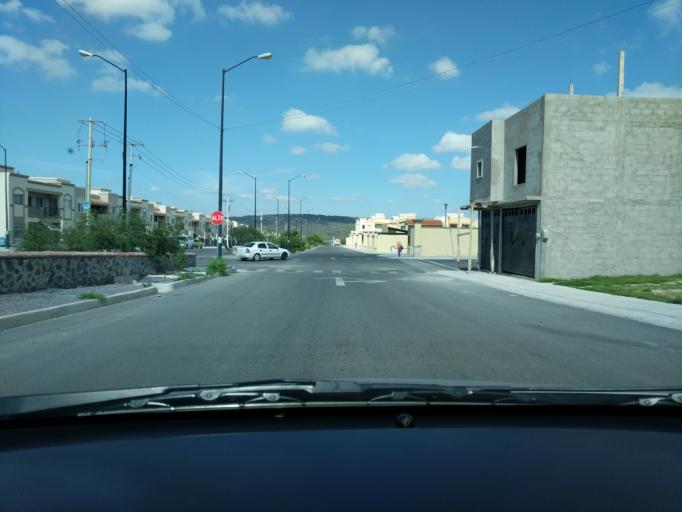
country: MX
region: Queretaro
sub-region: Queretaro
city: Patria Nueva
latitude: 20.6478
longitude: -100.4858
